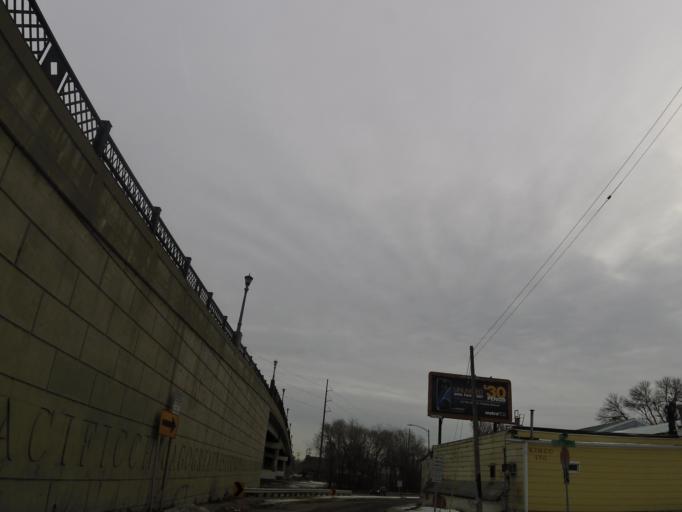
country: US
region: Minnesota
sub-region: Ramsey County
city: Falcon Heights
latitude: 44.9466
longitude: -93.1621
